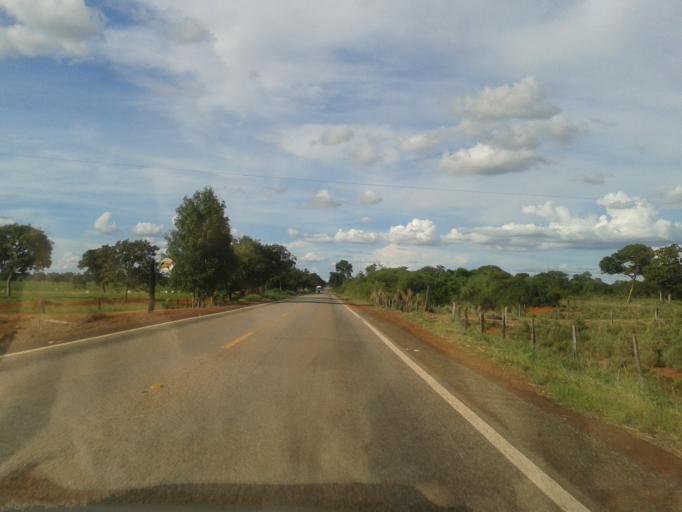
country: BR
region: Goias
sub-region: Mozarlandia
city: Mozarlandia
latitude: -14.2954
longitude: -50.4030
